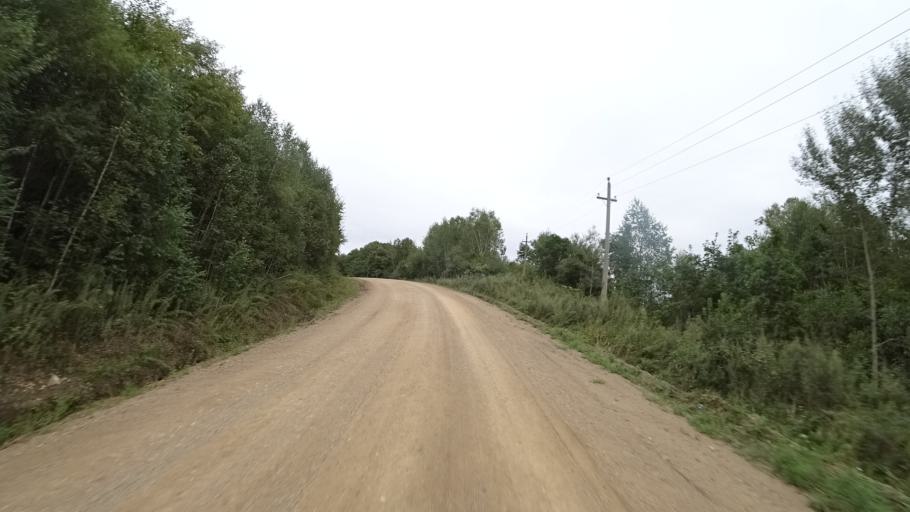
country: RU
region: Primorskiy
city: Rettikhovka
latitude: 44.1756
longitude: 132.8408
